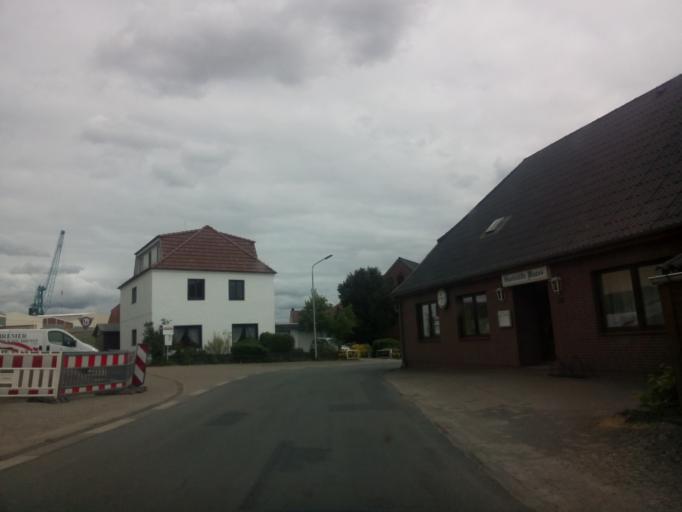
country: DE
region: Lower Saxony
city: Lemwerder
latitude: 53.1680
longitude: 8.6050
